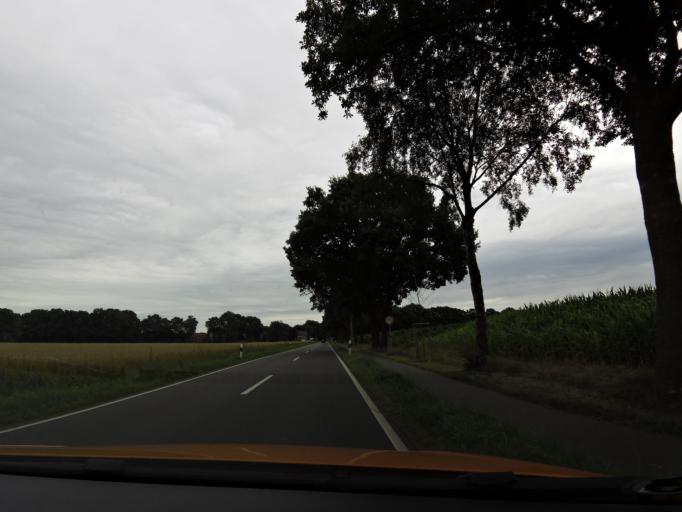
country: DE
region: Lower Saxony
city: Wiefelstede
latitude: 53.1901
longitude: 8.1491
